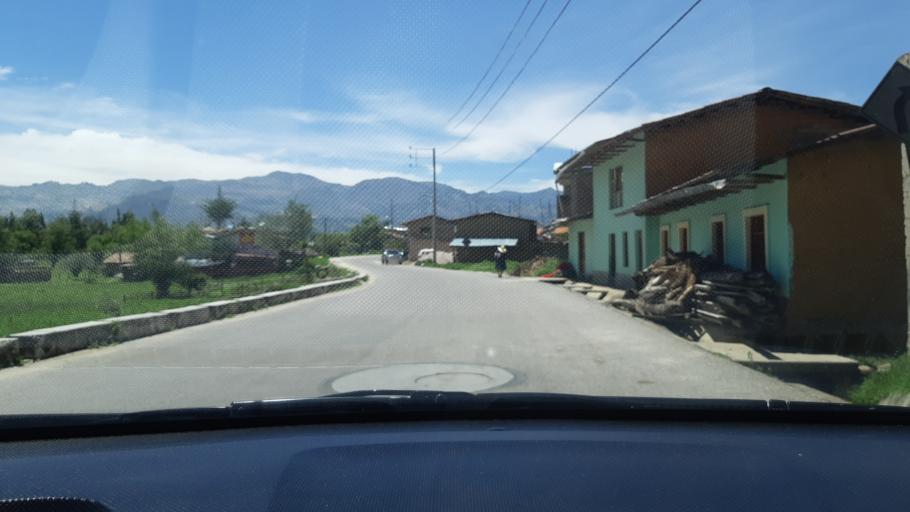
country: PE
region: Cajamarca
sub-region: Provincia de Cajamarca
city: Llacanora
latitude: -7.1828
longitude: -78.4463
